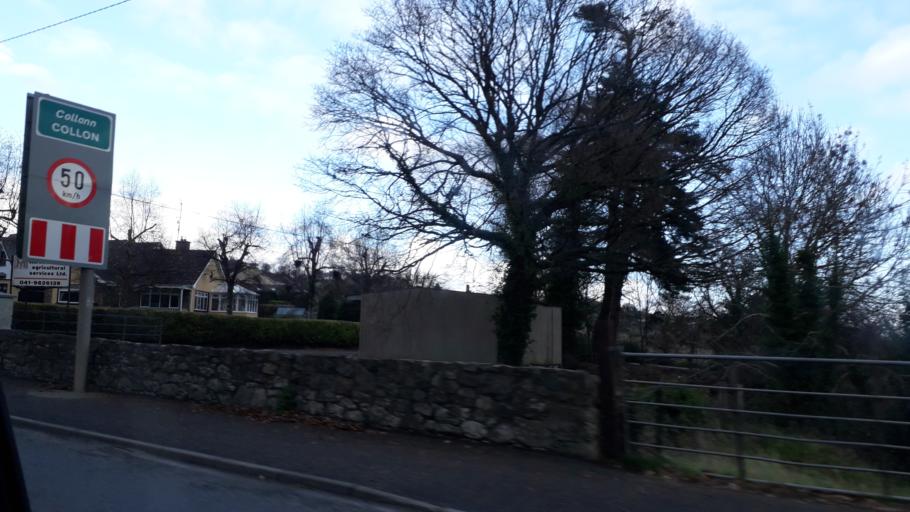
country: IE
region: Leinster
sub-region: Lu
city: Tullyallen
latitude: 53.7759
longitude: -6.4874
